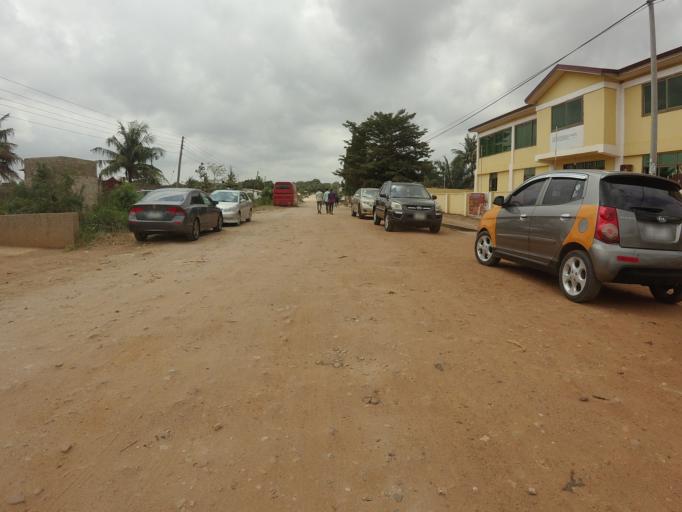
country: GH
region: Greater Accra
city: Dome
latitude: 5.6505
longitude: -0.2621
